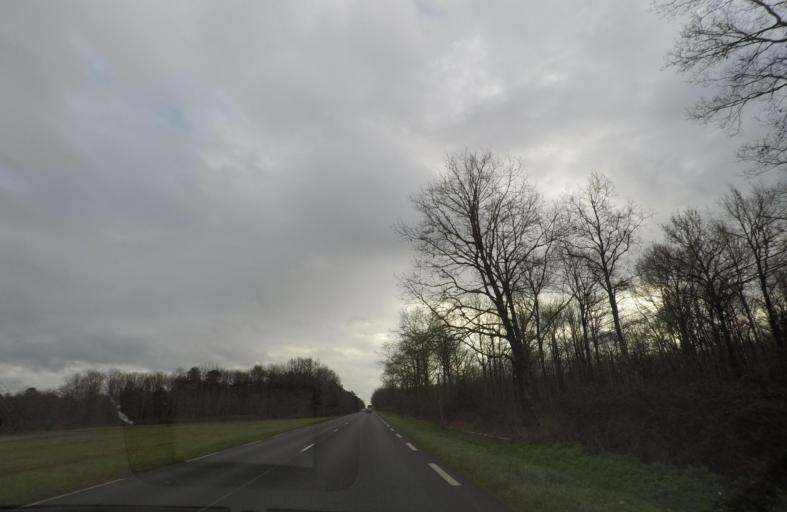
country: FR
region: Centre
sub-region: Departement du Loir-et-Cher
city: Mur-de-Sologne
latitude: 47.4218
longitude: 1.5858
